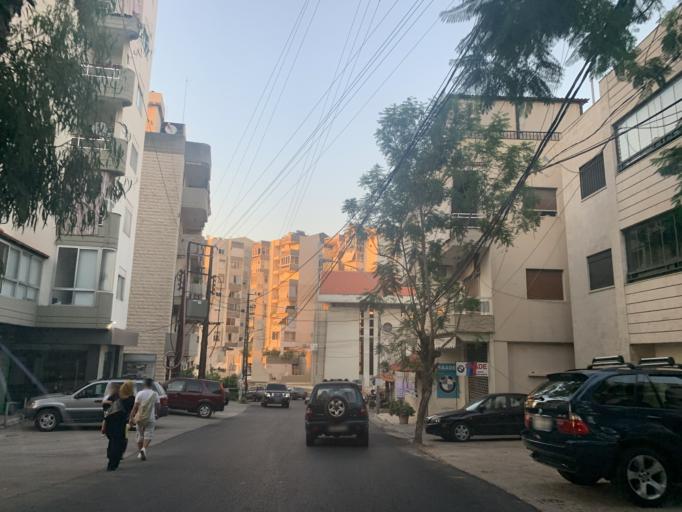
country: LB
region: Mont-Liban
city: Djounie
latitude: 33.9747
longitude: 35.6283
